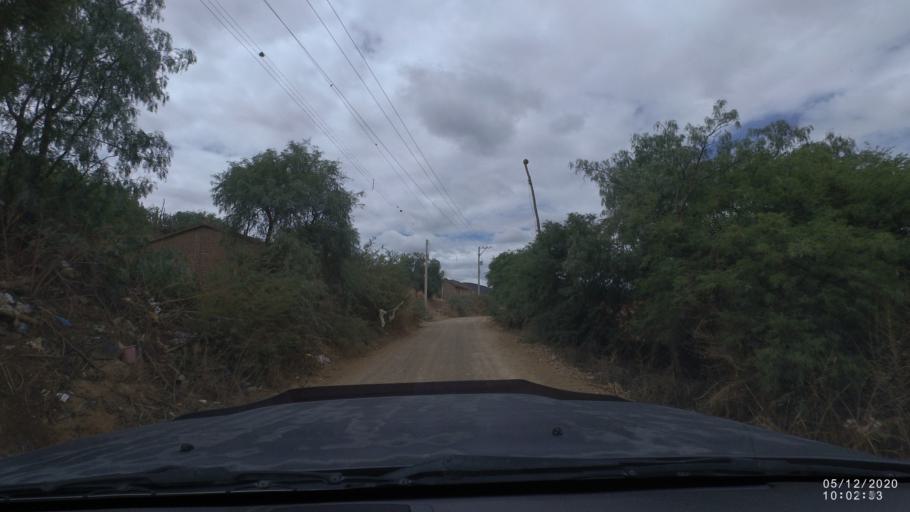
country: BO
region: Cochabamba
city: Sipe Sipe
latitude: -17.4537
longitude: -66.2858
